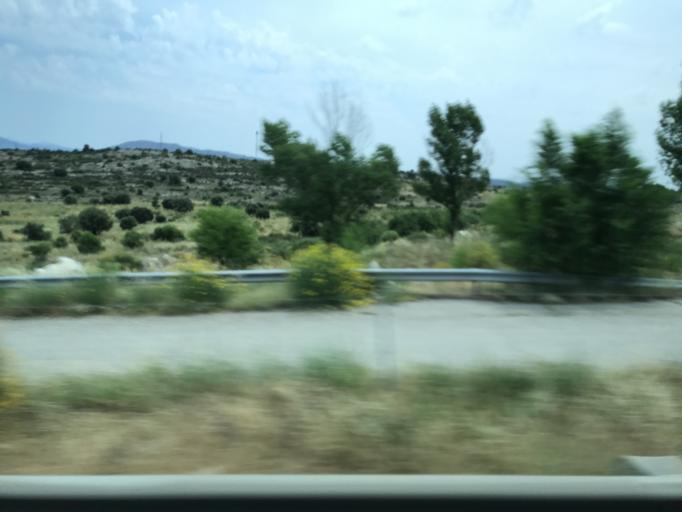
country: ES
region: Madrid
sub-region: Provincia de Madrid
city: La Cabrera
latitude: 40.8797
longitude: -3.5990
